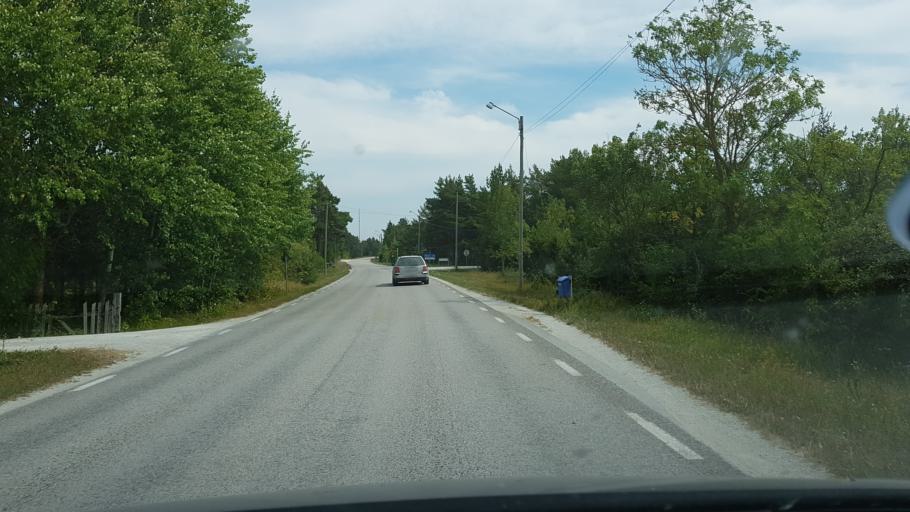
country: SE
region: Gotland
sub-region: Gotland
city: Slite
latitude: 57.7300
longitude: 18.7452
